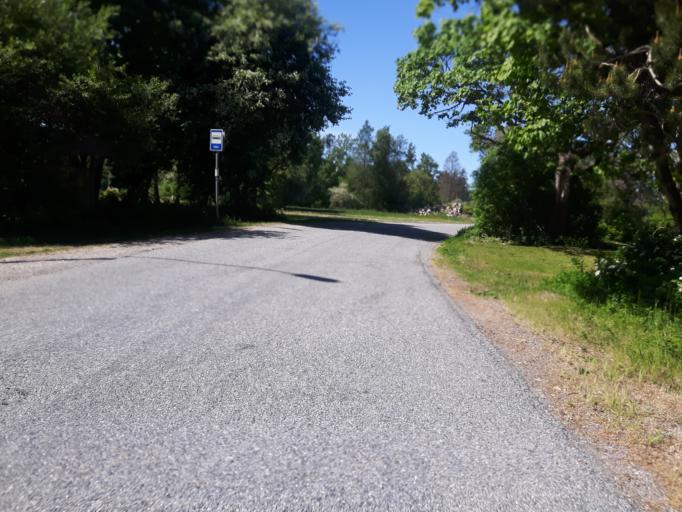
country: EE
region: Laeaene-Virumaa
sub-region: Haljala vald
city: Haljala
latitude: 59.5668
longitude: 26.2999
